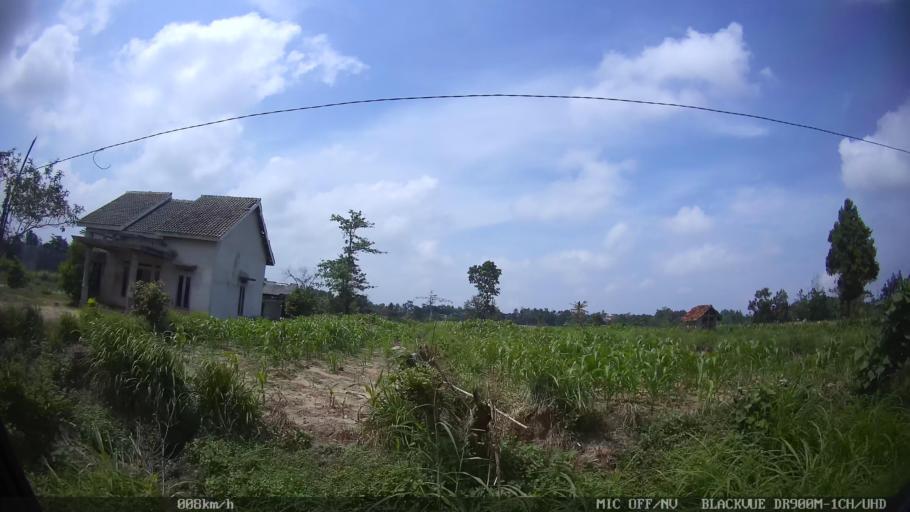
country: ID
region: Lampung
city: Kedaton
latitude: -5.3314
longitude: 105.2985
